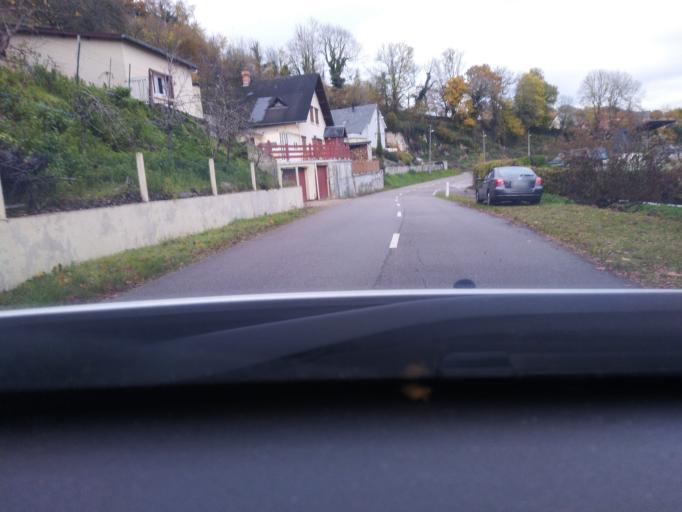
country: FR
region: Haute-Normandie
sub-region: Departement de la Seine-Maritime
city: Duclair
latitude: 49.4831
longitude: 0.8704
